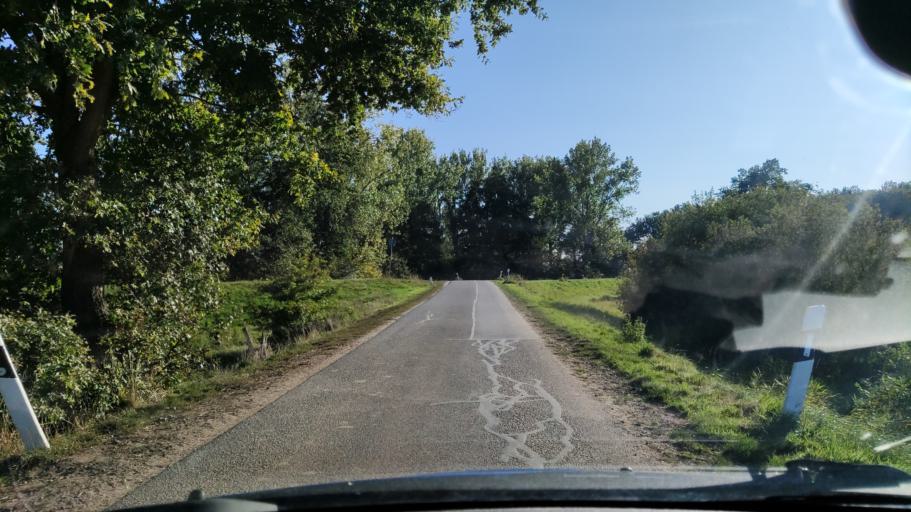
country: DE
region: Lower Saxony
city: Dannenberg
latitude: 53.1246
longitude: 11.0996
